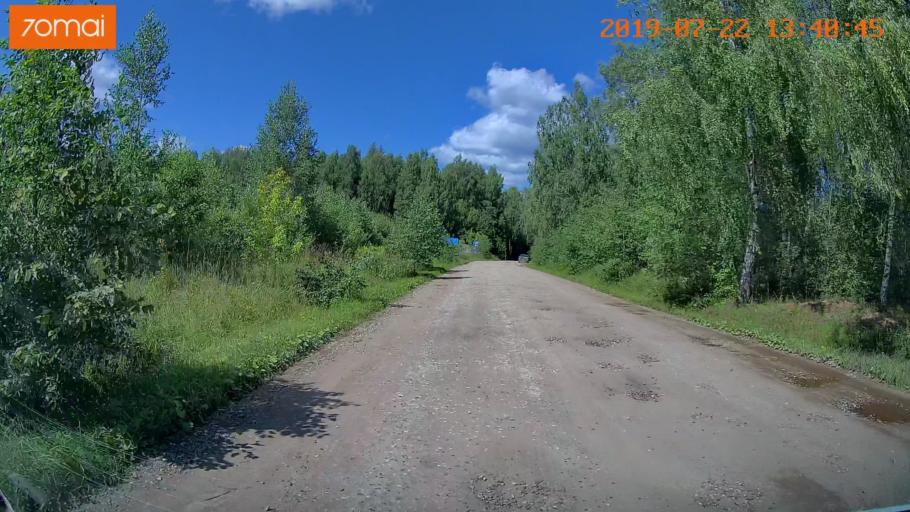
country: RU
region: Ivanovo
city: Novo-Talitsy
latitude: 57.0774
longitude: 40.8807
